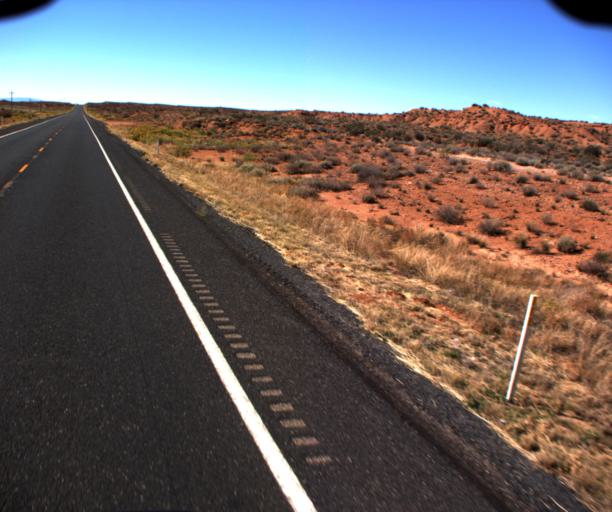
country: US
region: Arizona
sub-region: Coconino County
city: Fredonia
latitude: 36.9163
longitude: -112.5794
